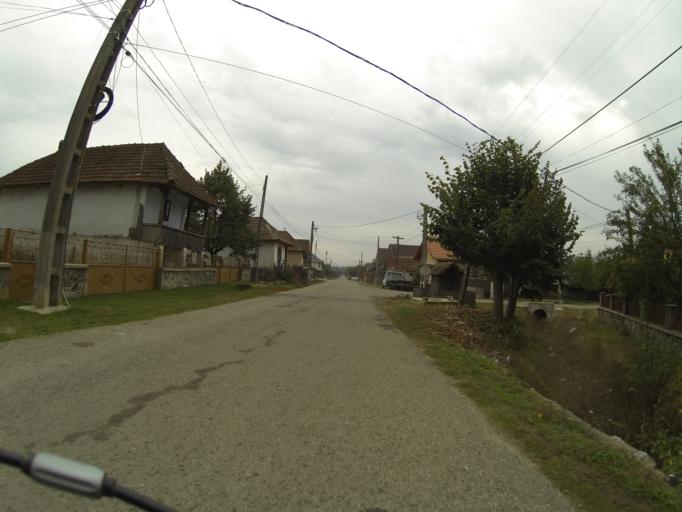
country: RO
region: Gorj
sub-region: Comuna Tismana
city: Pocruia
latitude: 45.0482
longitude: 22.9211
